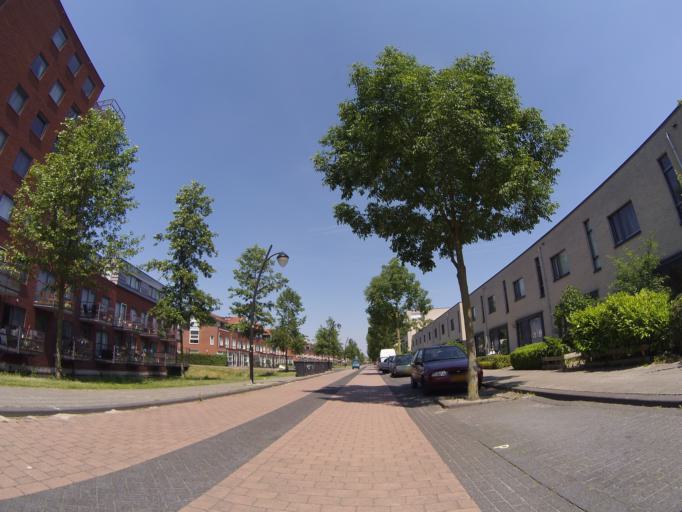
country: NL
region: Utrecht
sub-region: Gemeente Amersfoort
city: Hoogland
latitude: 52.1962
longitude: 5.4194
